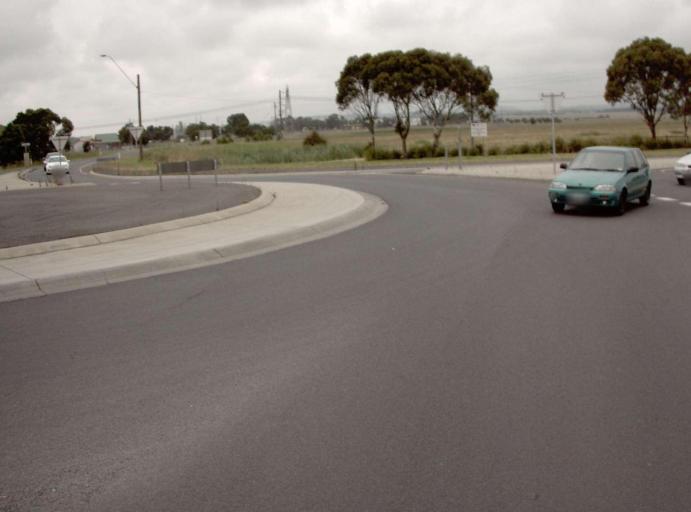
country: AU
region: Victoria
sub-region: Latrobe
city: Morwell
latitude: -38.2475
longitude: 146.4262
